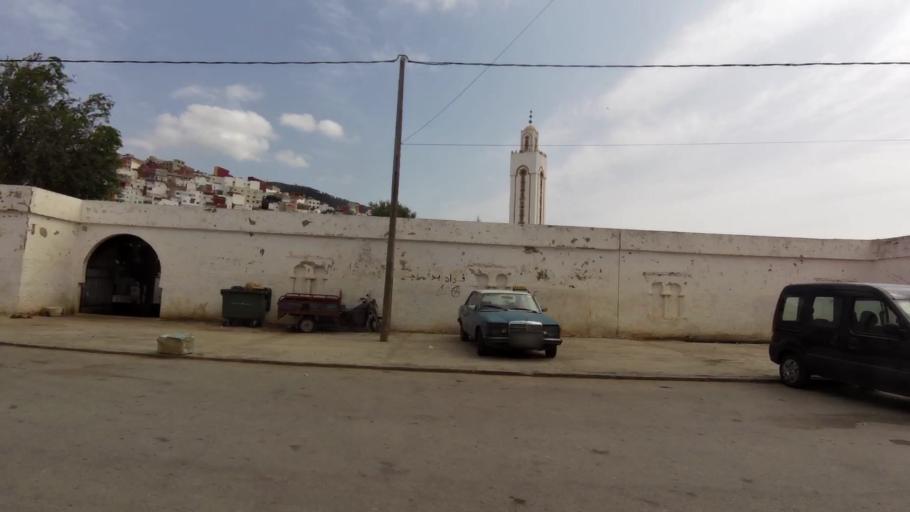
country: MA
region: Tanger-Tetouan
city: Tetouan
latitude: 35.5742
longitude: -5.3962
